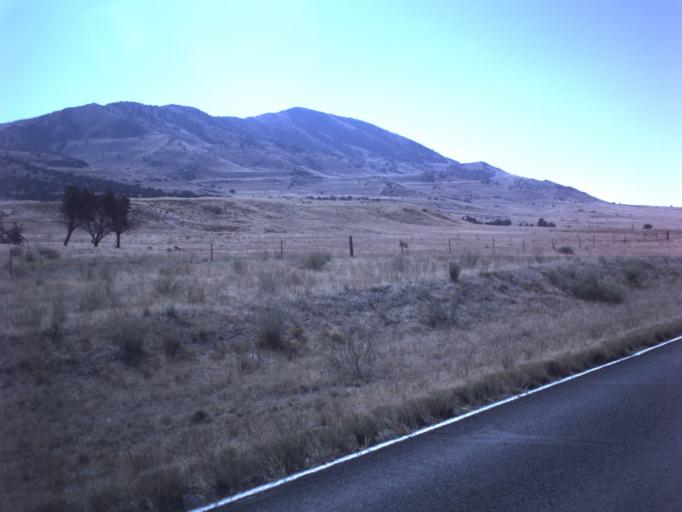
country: US
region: Utah
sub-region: Tooele County
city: Grantsville
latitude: 40.5803
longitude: -112.7257
